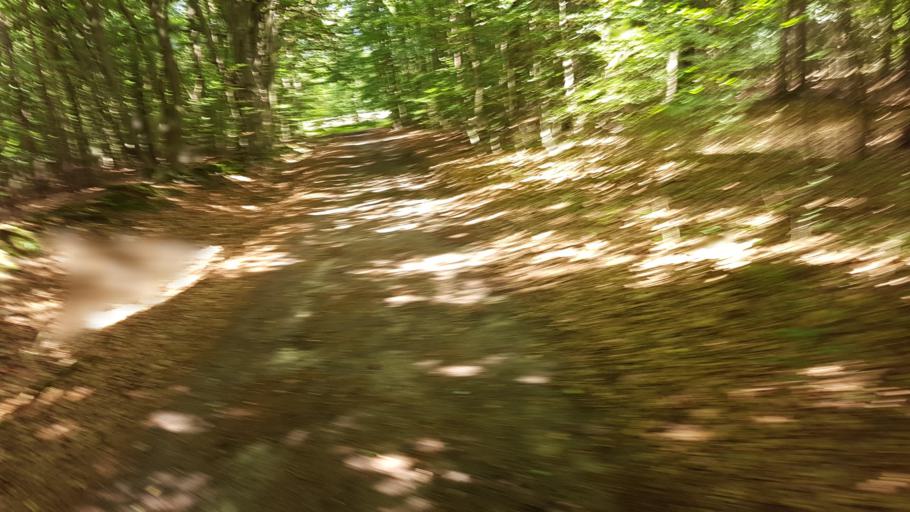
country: DE
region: Lower Saxony
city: Rullstorf
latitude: 53.2843
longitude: 10.5433
